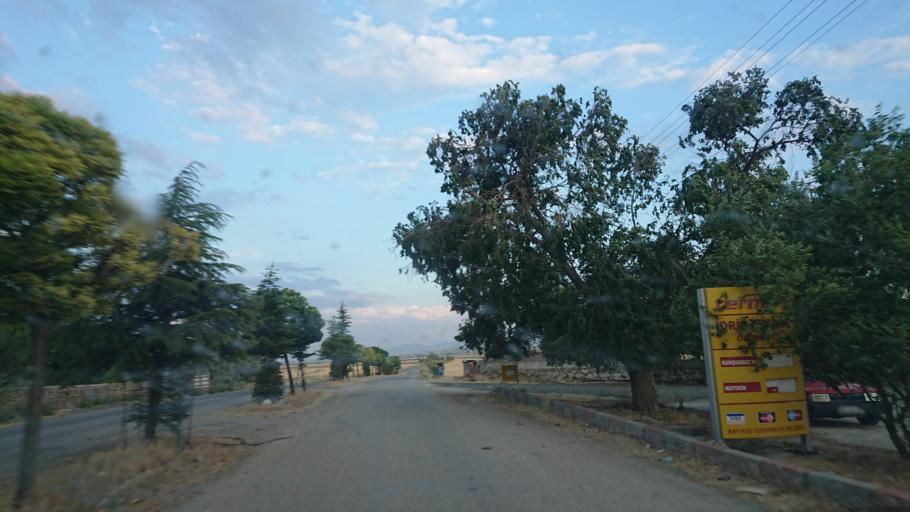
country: TR
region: Aksaray
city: Agacoren
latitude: 38.9209
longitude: 34.0352
